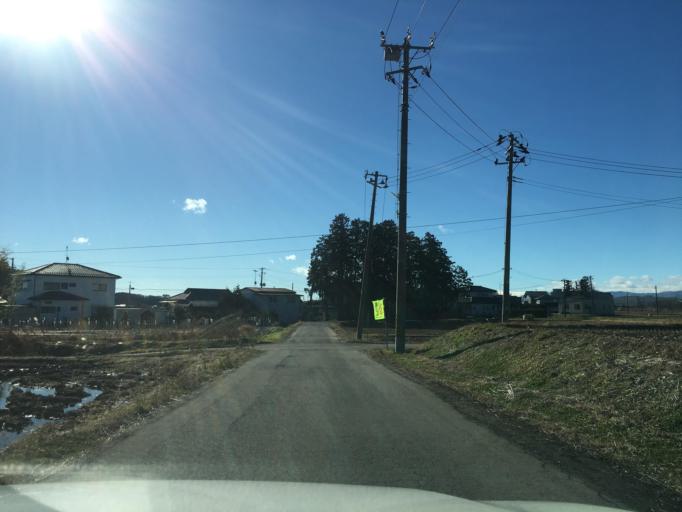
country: JP
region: Fukushima
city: Motomiya
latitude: 37.4877
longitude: 140.3944
